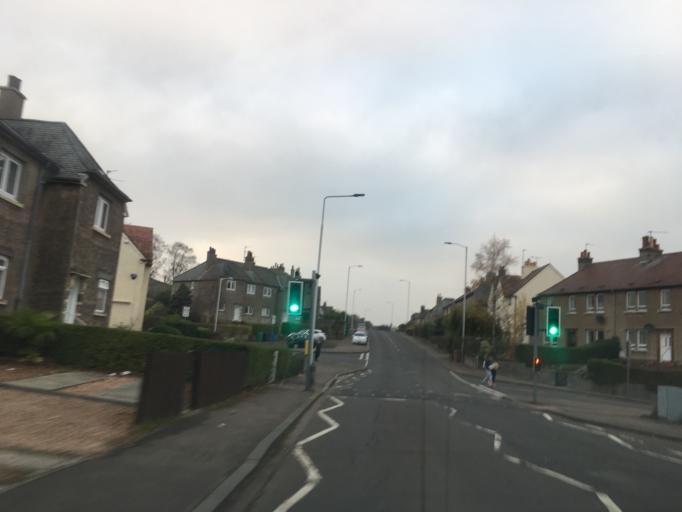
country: GB
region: Scotland
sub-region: Fife
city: Saint Andrews
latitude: 56.3331
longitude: -2.7984
